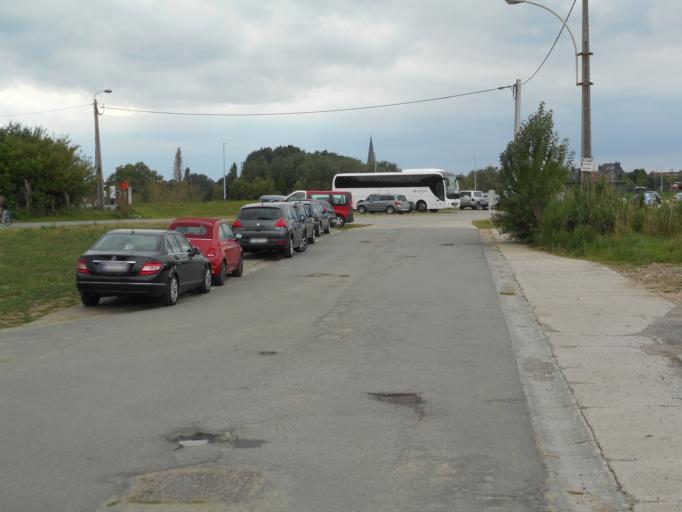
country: BE
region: Flanders
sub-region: Provincie Oost-Vlaanderen
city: Kruibeke
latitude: 51.1759
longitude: 4.3243
